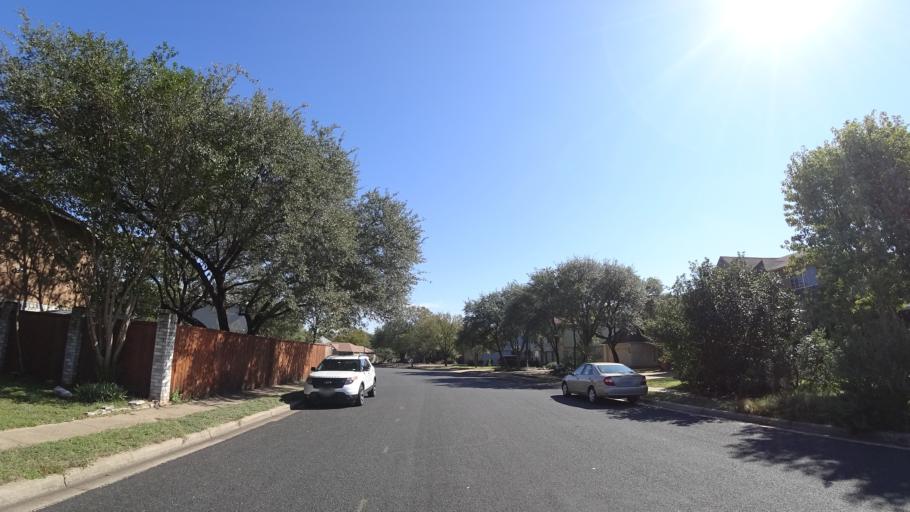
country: US
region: Texas
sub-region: Travis County
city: Shady Hollow
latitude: 30.2139
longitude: -97.8744
